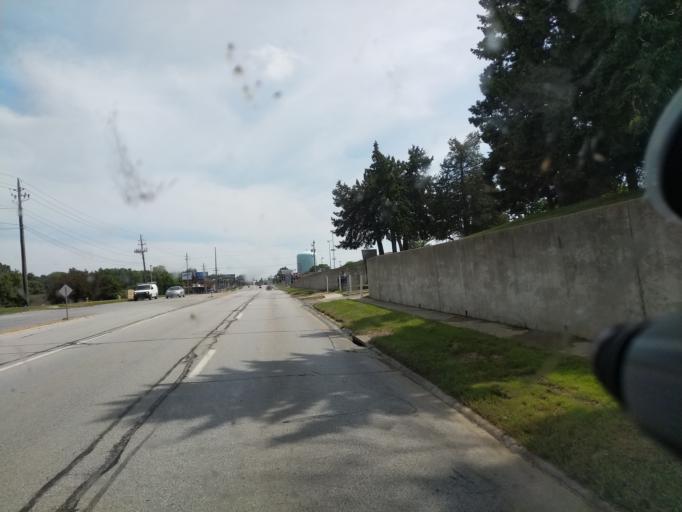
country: US
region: Iowa
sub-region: Polk County
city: Urbandale
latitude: 41.6389
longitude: -93.6977
